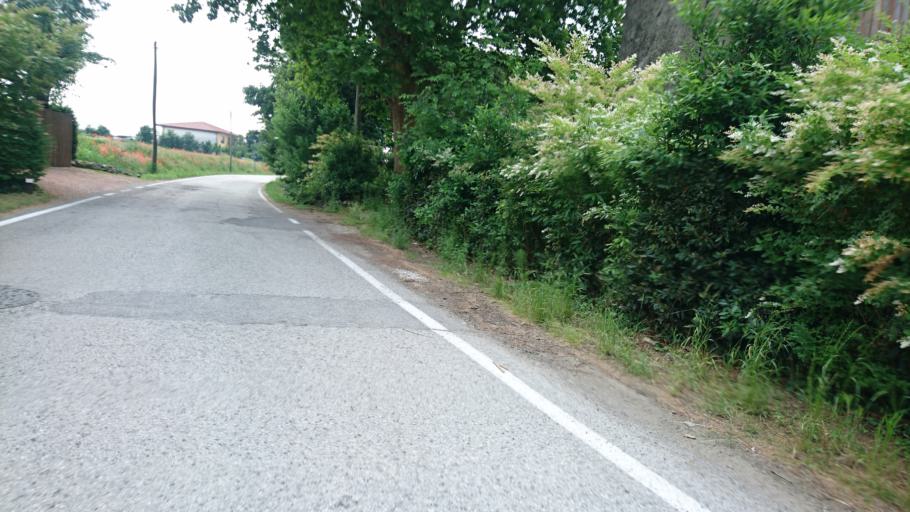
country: IT
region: Veneto
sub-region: Provincia di Padova
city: Cartura
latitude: 45.2595
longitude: 11.8807
